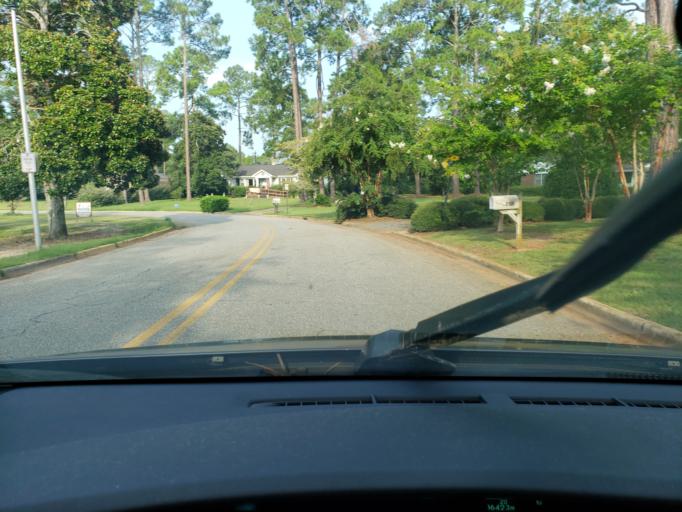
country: US
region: Georgia
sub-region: Dougherty County
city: Albany
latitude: 31.6003
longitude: -84.2027
